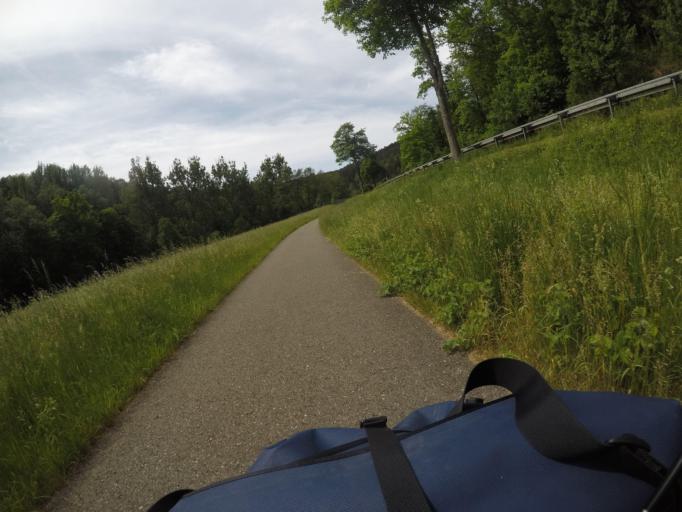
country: DE
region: Baden-Wuerttemberg
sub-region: Karlsruhe Region
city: Rohrdorf
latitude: 48.5801
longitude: 8.7219
